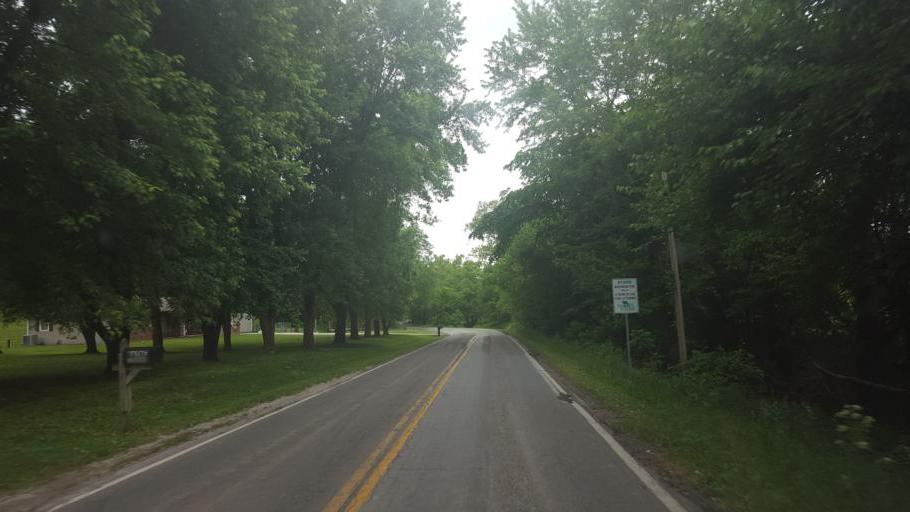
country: US
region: Missouri
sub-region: Moniteau County
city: California
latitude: 38.6490
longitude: -92.5715
